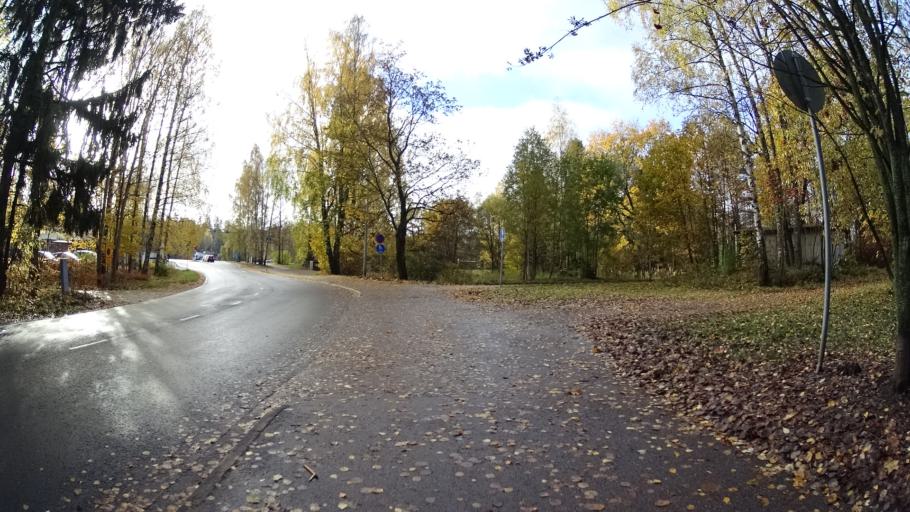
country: FI
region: Uusimaa
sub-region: Helsinki
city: Kauniainen
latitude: 60.2252
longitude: 24.7063
